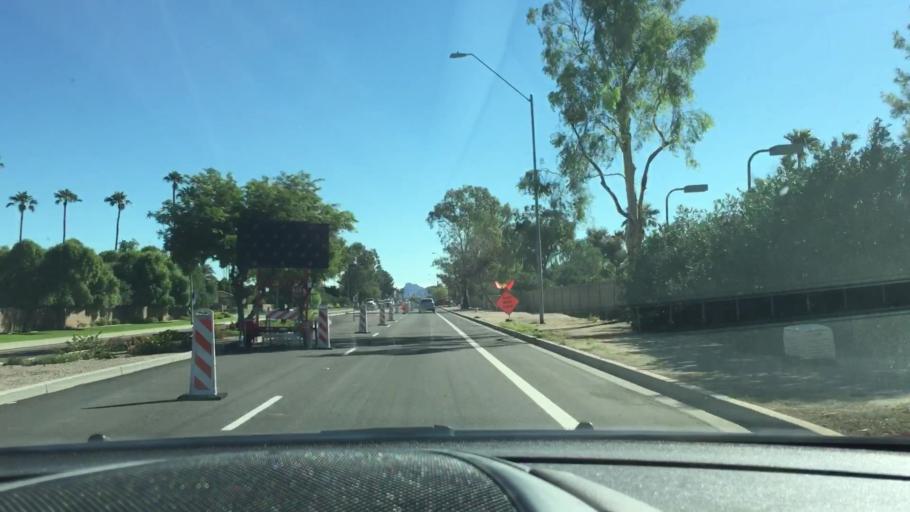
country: US
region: Arizona
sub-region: Maricopa County
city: Scottsdale
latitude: 33.5383
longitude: -111.8985
